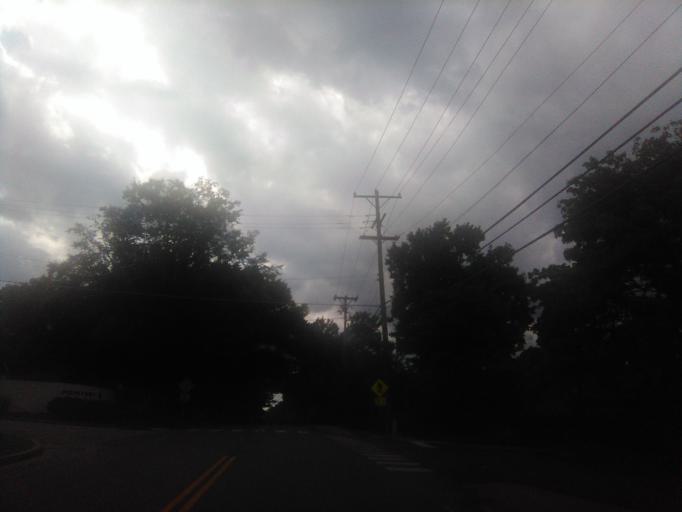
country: US
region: Tennessee
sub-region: Davidson County
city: Belle Meade
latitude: 36.1090
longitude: -86.8301
